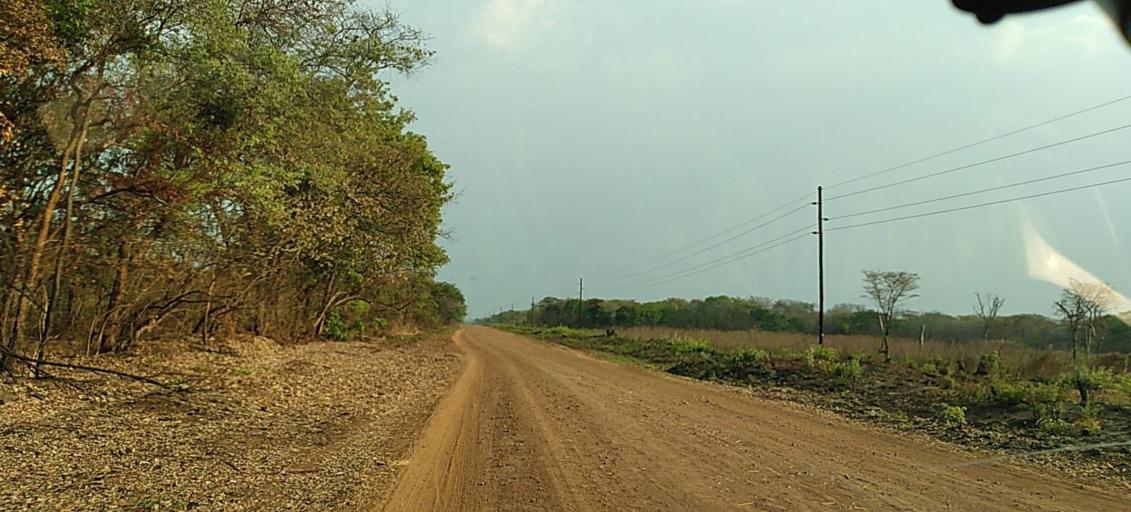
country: ZM
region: Western
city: Lukulu
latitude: -14.0002
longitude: 23.6173
